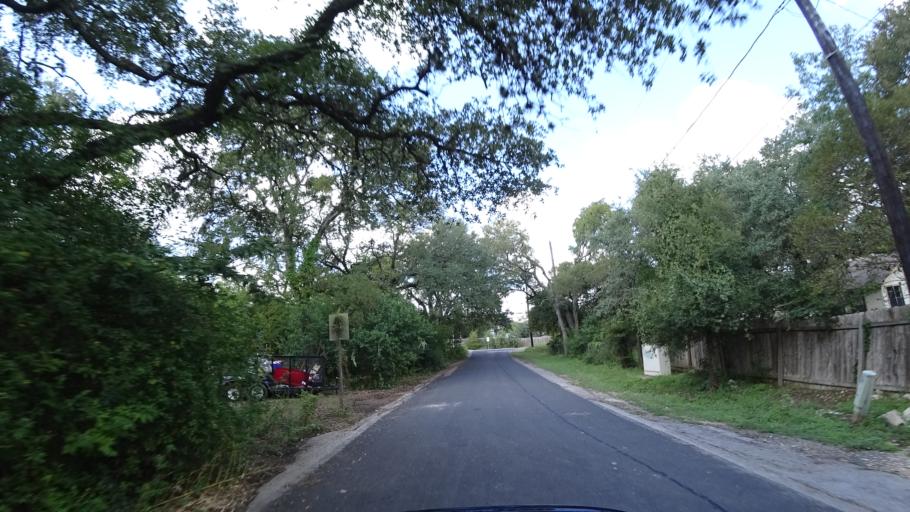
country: US
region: Texas
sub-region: Travis County
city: Manchaca
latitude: 30.1951
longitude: -97.8097
